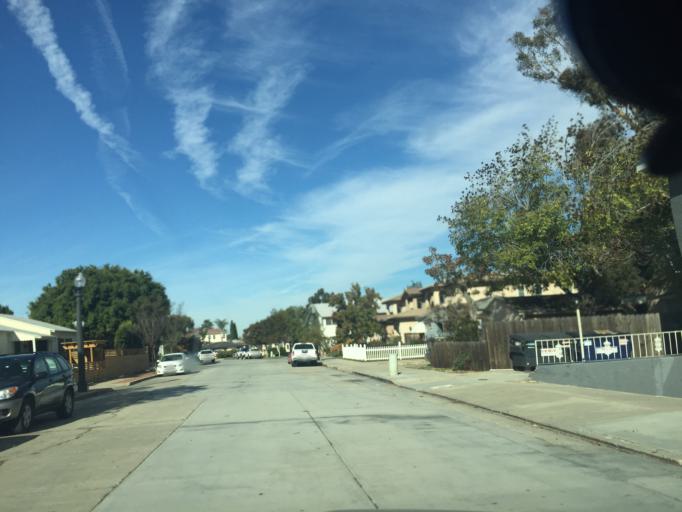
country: US
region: California
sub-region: San Diego County
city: Lemon Grove
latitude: 32.7597
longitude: -117.0825
